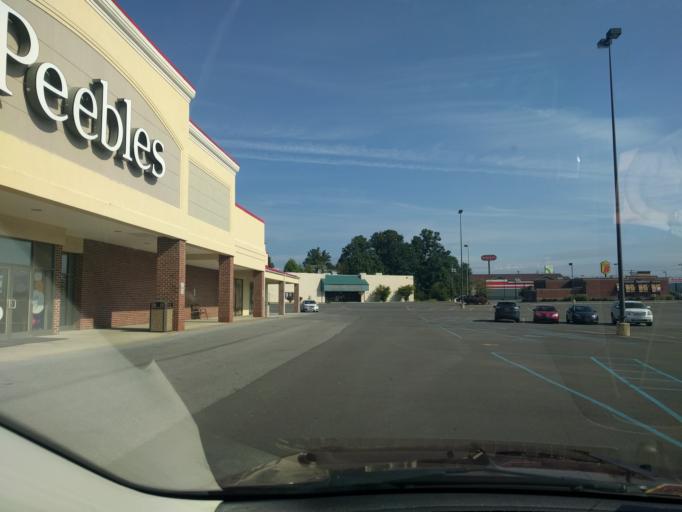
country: US
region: West Virginia
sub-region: Nicholas County
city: Summersville
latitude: 38.2993
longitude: -80.8351
